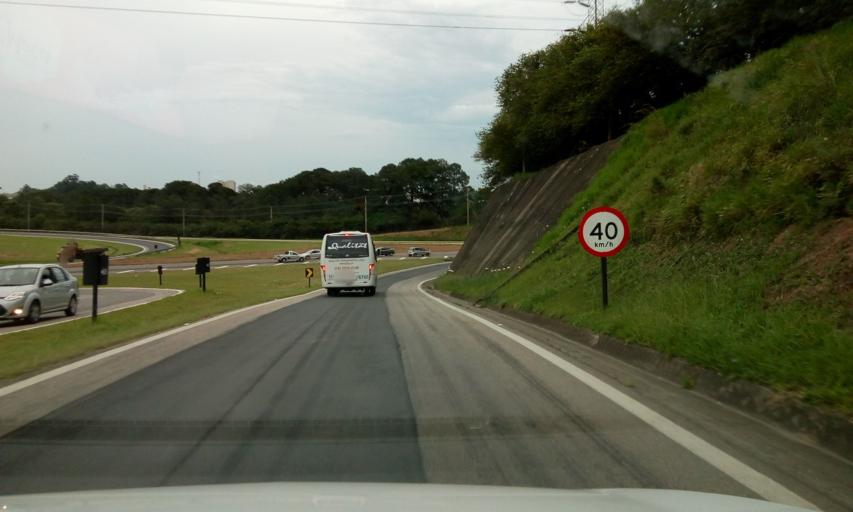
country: BR
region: Sao Paulo
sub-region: Jundiai
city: Jundiai
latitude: -23.1825
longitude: -46.9690
